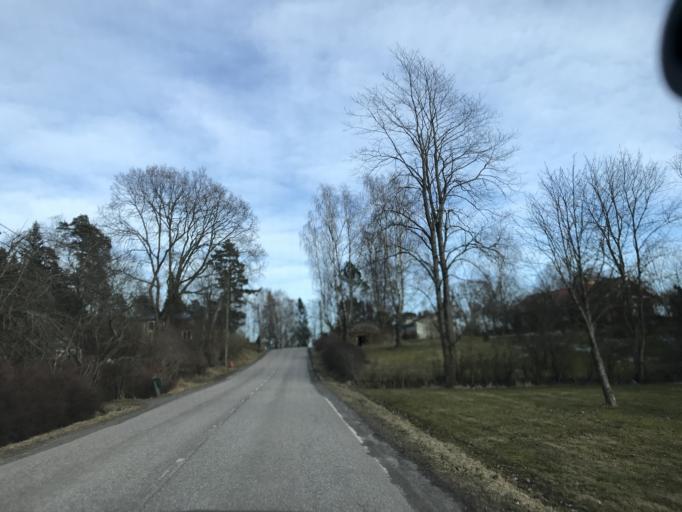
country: FI
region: Uusimaa
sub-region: Raaseporin
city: Pohja
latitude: 60.0962
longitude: 23.5302
